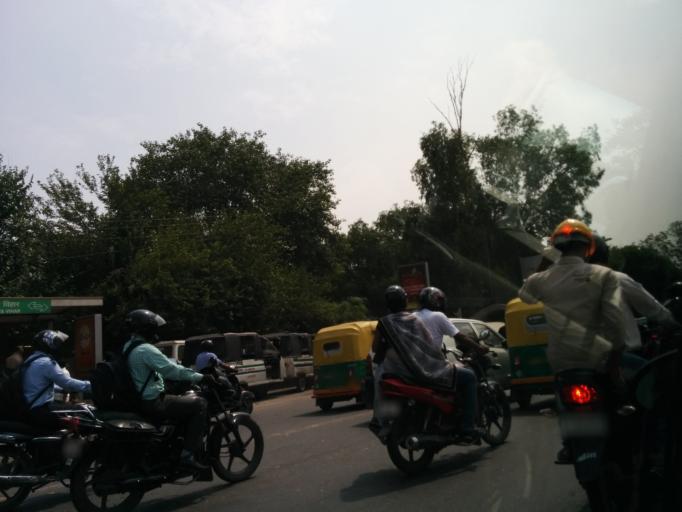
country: IN
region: NCT
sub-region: New Delhi
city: New Delhi
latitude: 28.5438
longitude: 77.2052
